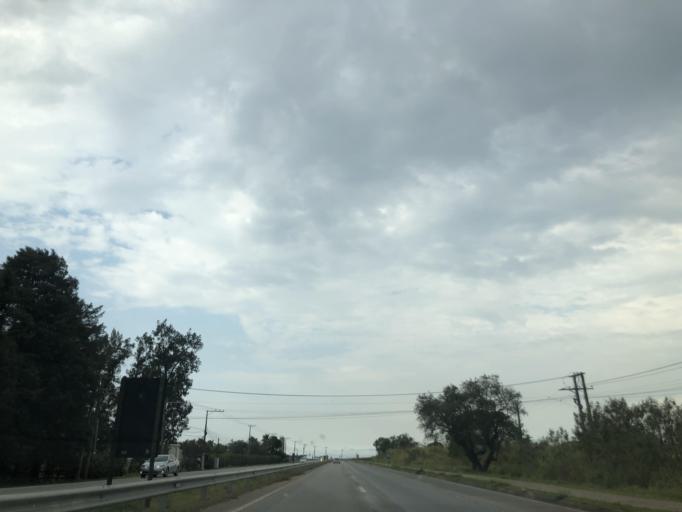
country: BR
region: Sao Paulo
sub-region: Salto De Pirapora
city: Salto de Pirapora
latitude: -23.5784
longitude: -47.5230
